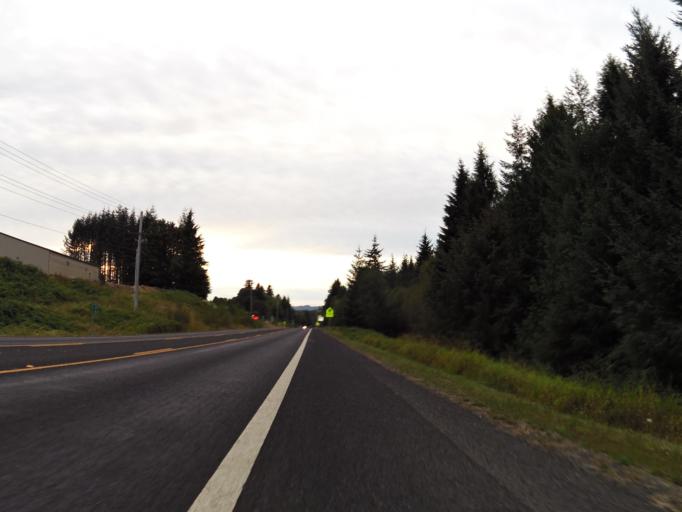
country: US
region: Washington
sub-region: Wahkiakum County
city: Cathlamet
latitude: 46.2007
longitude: -123.3738
